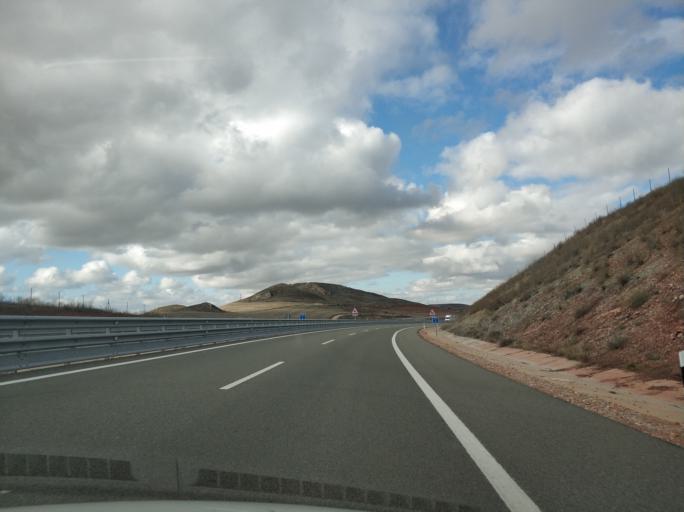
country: ES
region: Castille and Leon
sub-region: Provincia de Soria
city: Medinaceli
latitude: 41.1955
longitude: -2.4562
